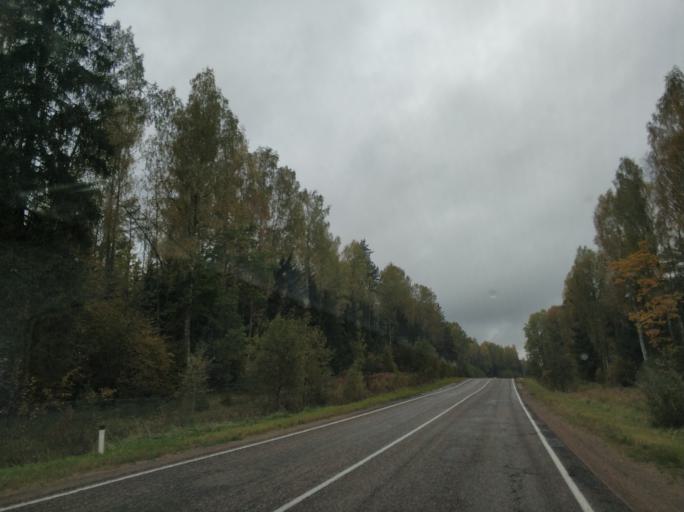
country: RU
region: Pskov
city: Opochka
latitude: 56.5181
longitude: 28.6600
